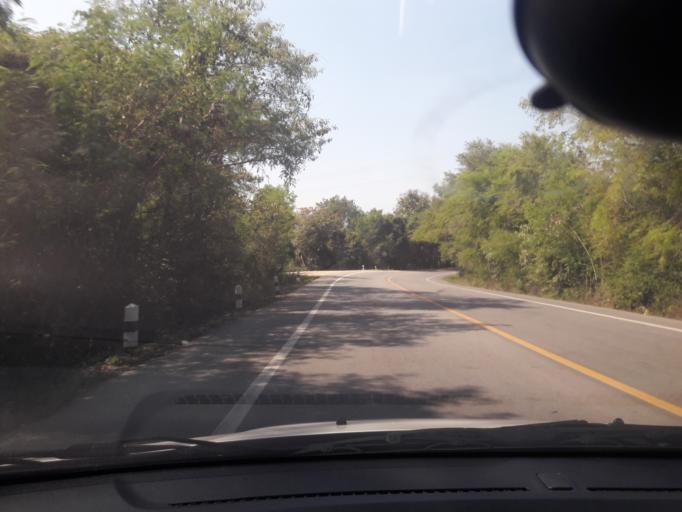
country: TH
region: Lampang
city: Mae Tha
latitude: 18.1874
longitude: 99.5457
